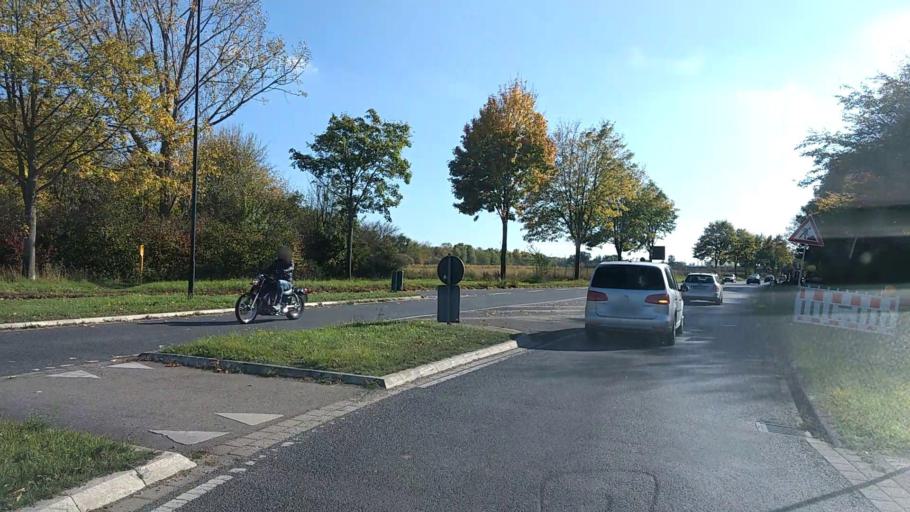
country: DE
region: North Rhine-Westphalia
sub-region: Regierungsbezirk Koln
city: Kerpen
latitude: 50.9112
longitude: 6.6841
